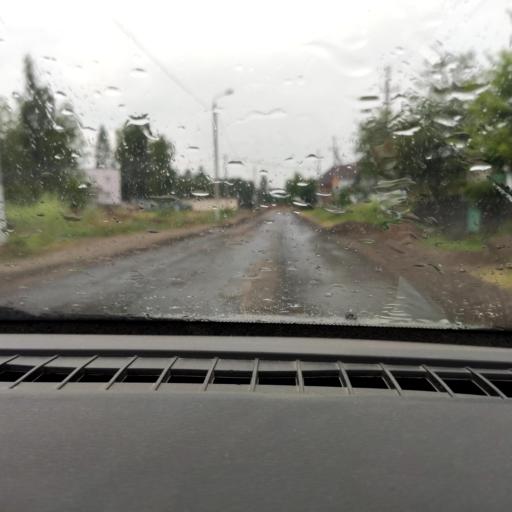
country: RU
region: Perm
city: Perm
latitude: 58.1032
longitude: 56.2896
